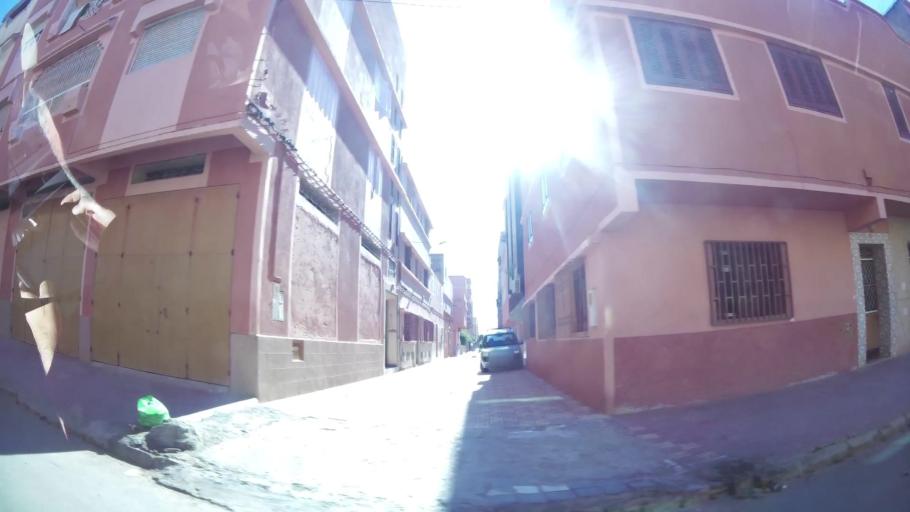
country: MA
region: Oriental
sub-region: Berkane-Taourirt
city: Berkane
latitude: 34.9330
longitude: -2.3327
